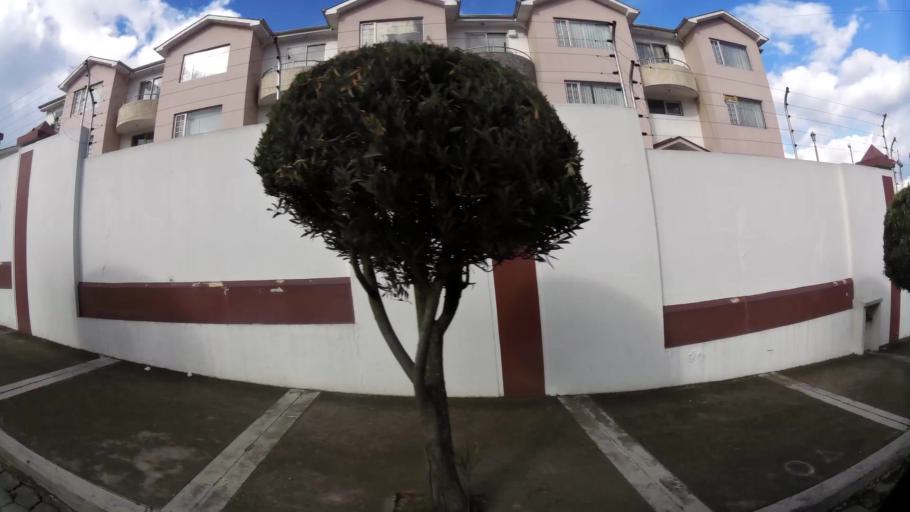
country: EC
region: Pichincha
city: Quito
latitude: -0.1333
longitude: -78.4718
